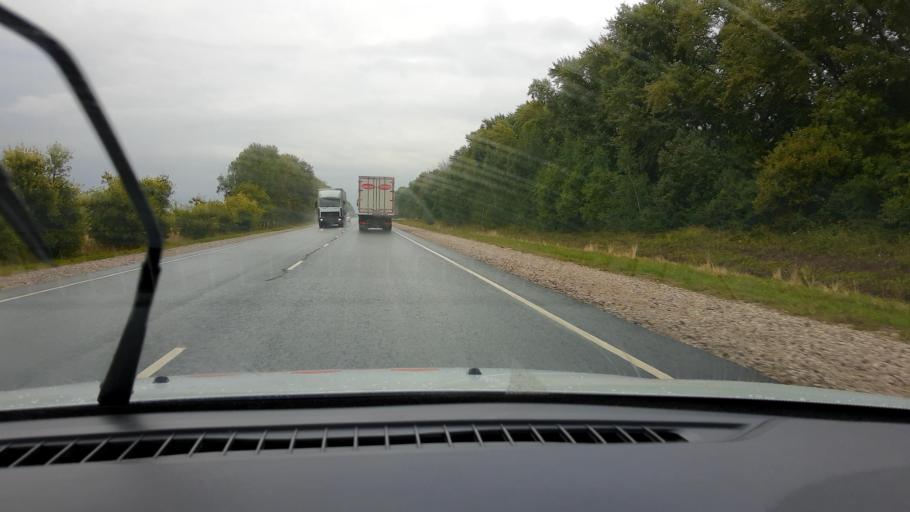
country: RU
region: Chuvashia
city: Yantikovo
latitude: 55.7895
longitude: 47.7060
